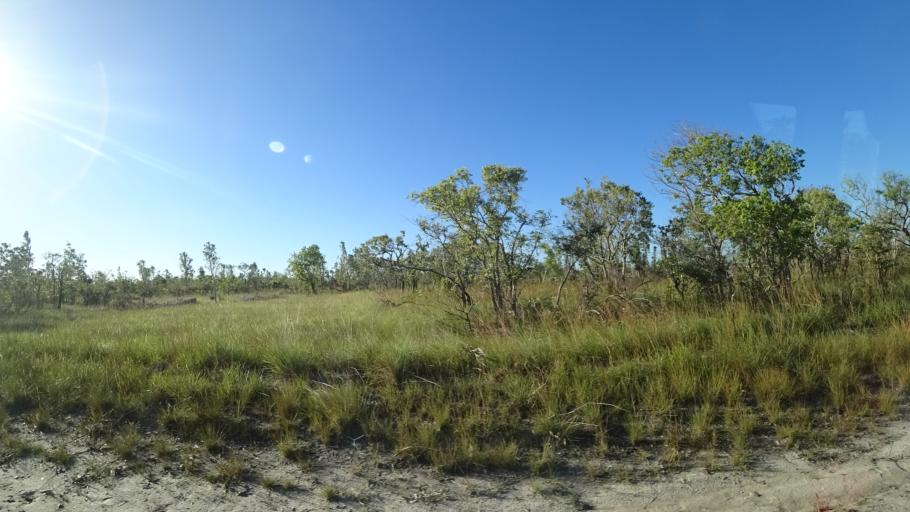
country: MZ
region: Sofala
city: Beira
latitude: -19.5753
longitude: 35.2523
